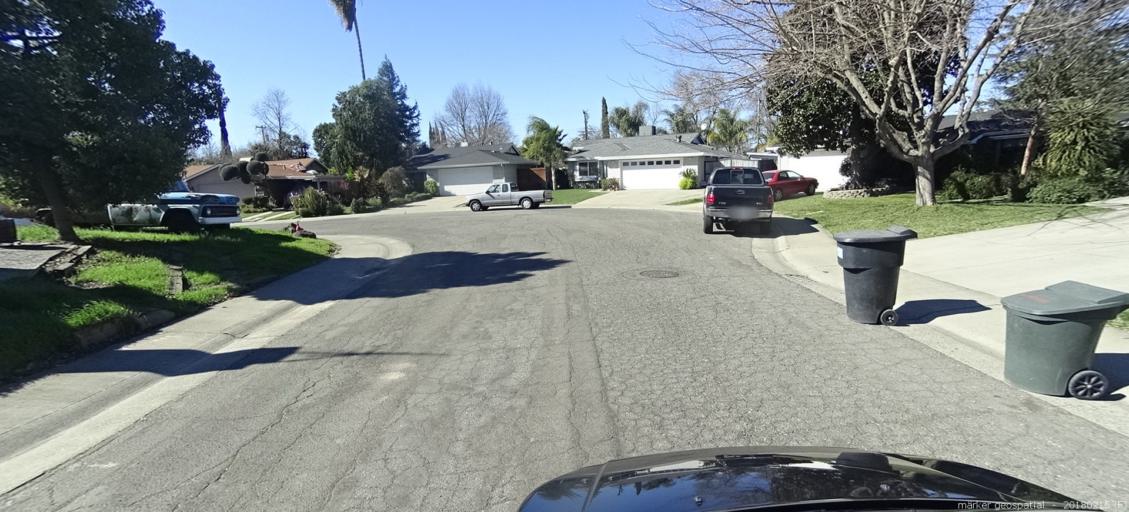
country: US
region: California
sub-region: Sacramento County
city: Foothill Farms
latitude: 38.6704
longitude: -121.3180
